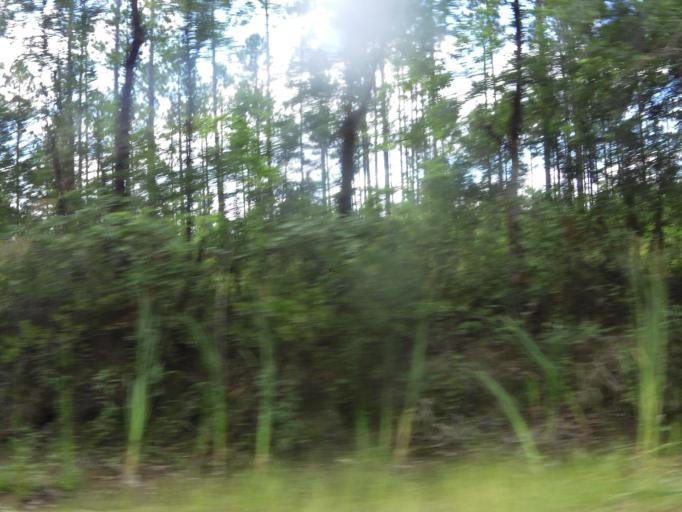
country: US
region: Florida
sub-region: Clay County
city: Asbury Lake
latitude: 29.8957
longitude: -81.8621
